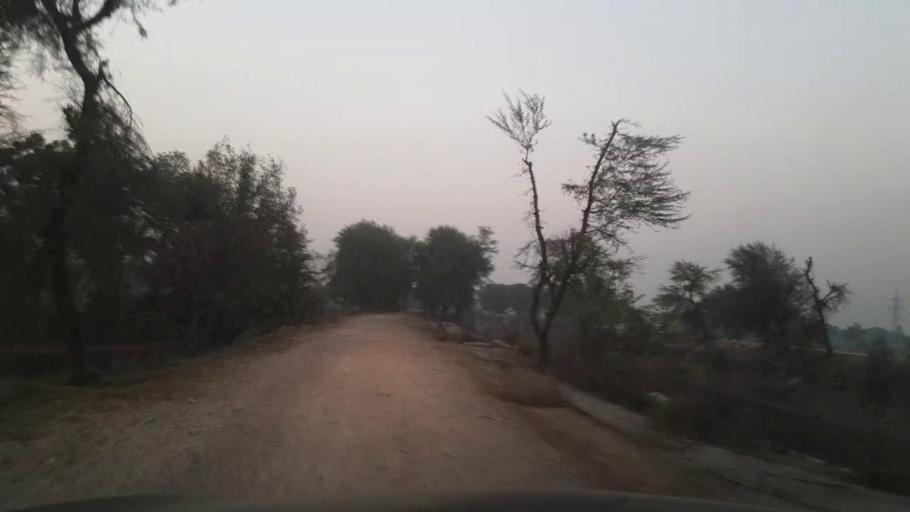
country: PK
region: Sindh
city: Ubauro
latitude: 28.1868
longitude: 69.7813
